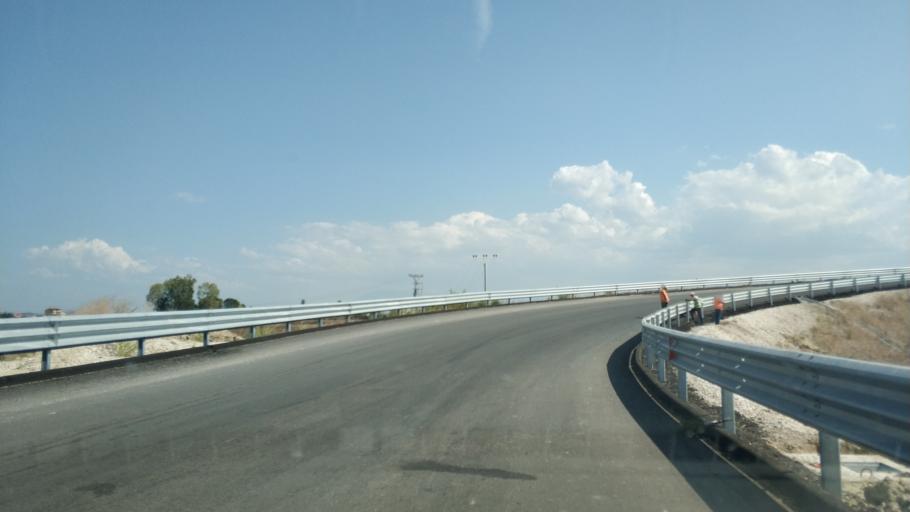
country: AL
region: Fier
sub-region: Rrethi i Fierit
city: Dermenas
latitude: 40.7414
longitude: 19.4824
